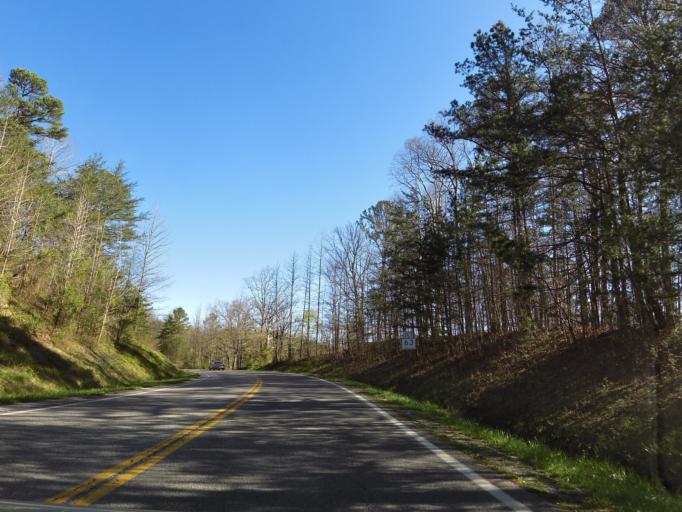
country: US
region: Tennessee
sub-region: Scott County
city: Huntsville
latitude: 36.4000
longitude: -84.4389
